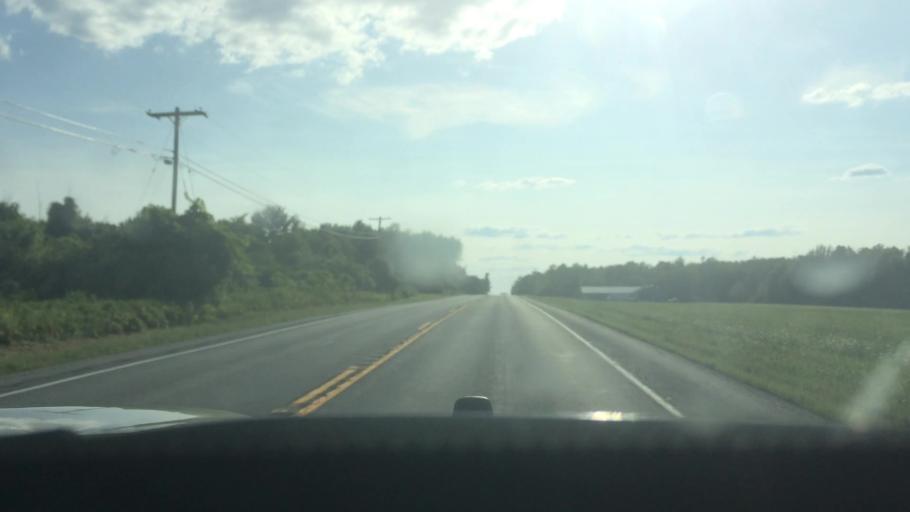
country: US
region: New York
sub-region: St. Lawrence County
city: Potsdam
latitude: 44.6814
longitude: -74.8204
